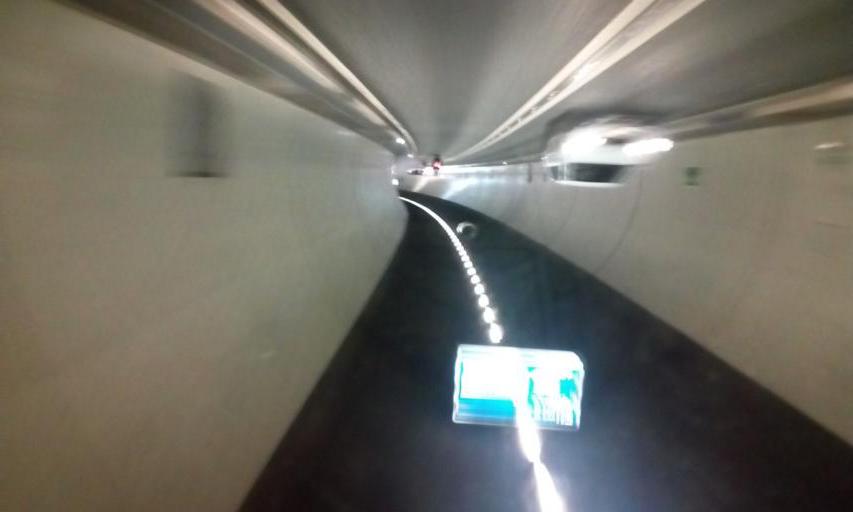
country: CH
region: Grisons
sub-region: Imboden District
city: Bonaduz
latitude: 46.8319
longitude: 9.3496
